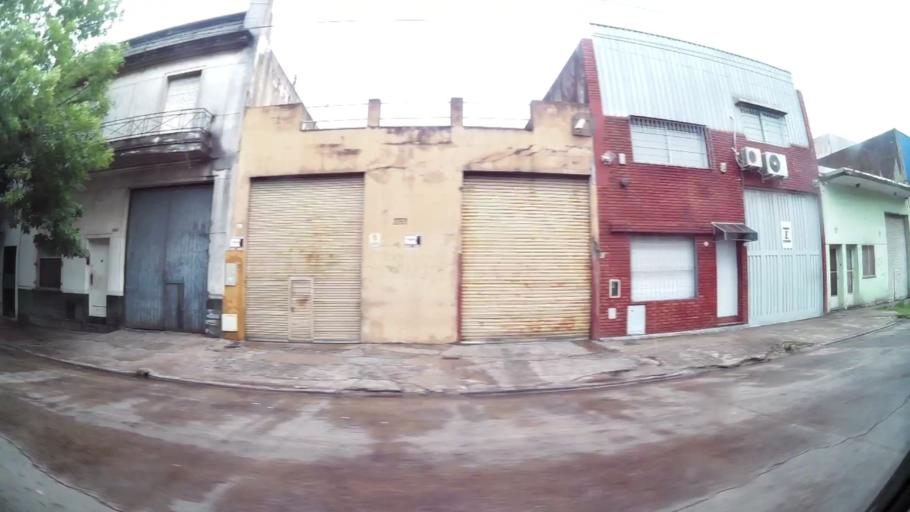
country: AR
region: Buenos Aires F.D.
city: Villa Lugano
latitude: -34.6589
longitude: -58.4437
